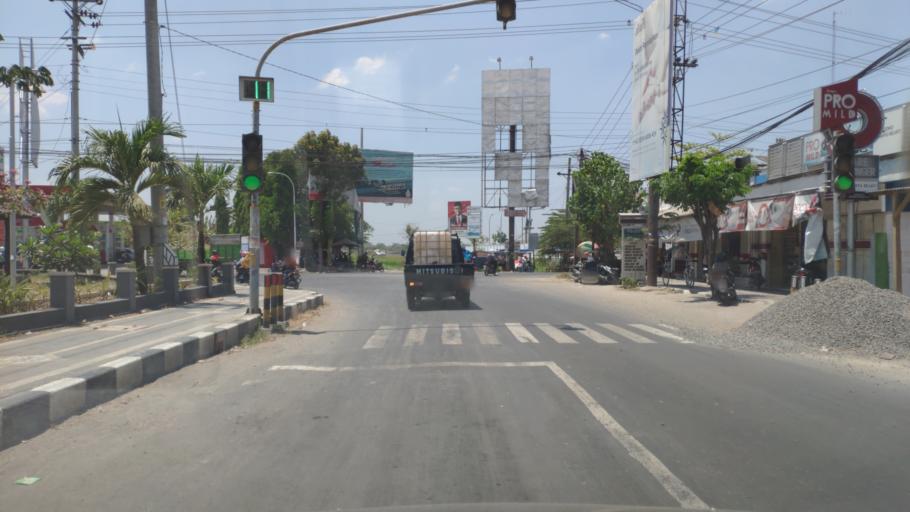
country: ID
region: Central Java
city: Cepu
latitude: -7.1536
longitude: 111.5811
